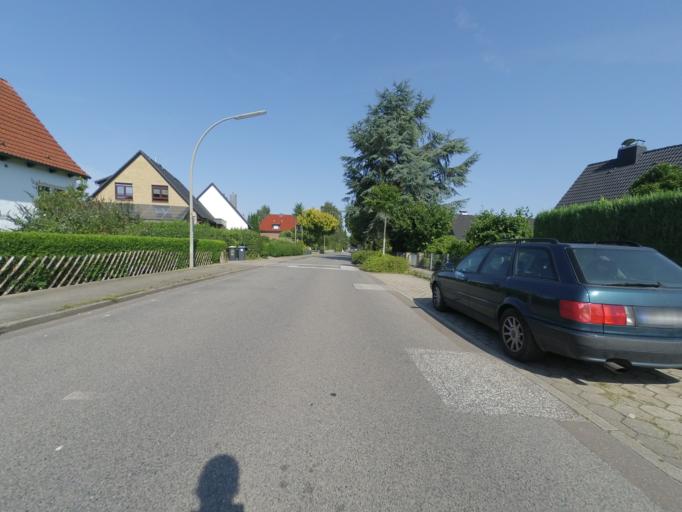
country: DE
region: Schleswig-Holstein
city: Glinde
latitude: 53.4975
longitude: 10.1771
